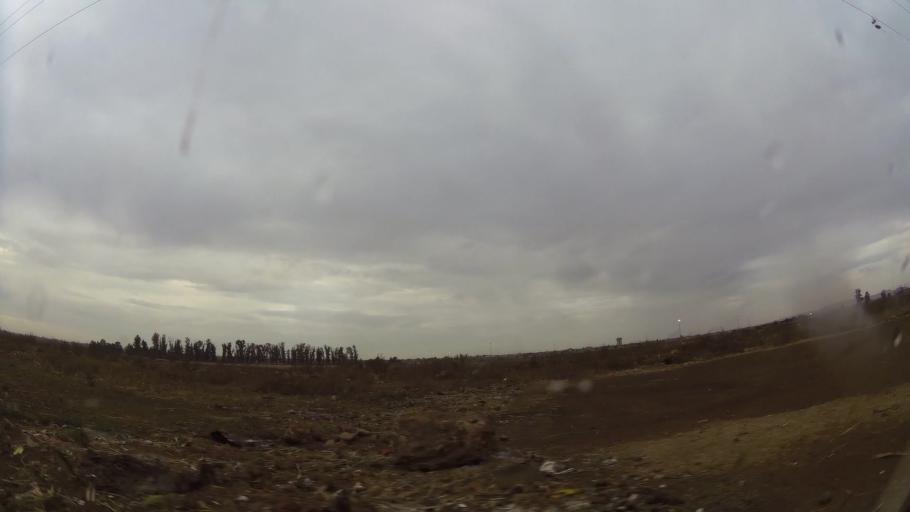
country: ZA
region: Gauteng
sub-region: Ekurhuleni Metropolitan Municipality
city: Germiston
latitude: -26.3709
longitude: 28.1714
